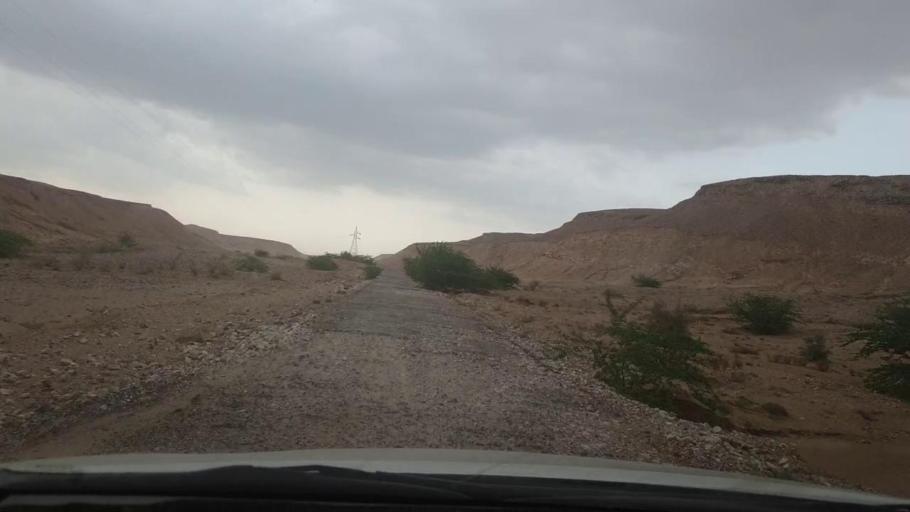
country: PK
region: Sindh
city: Khairpur
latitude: 27.4649
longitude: 68.9245
